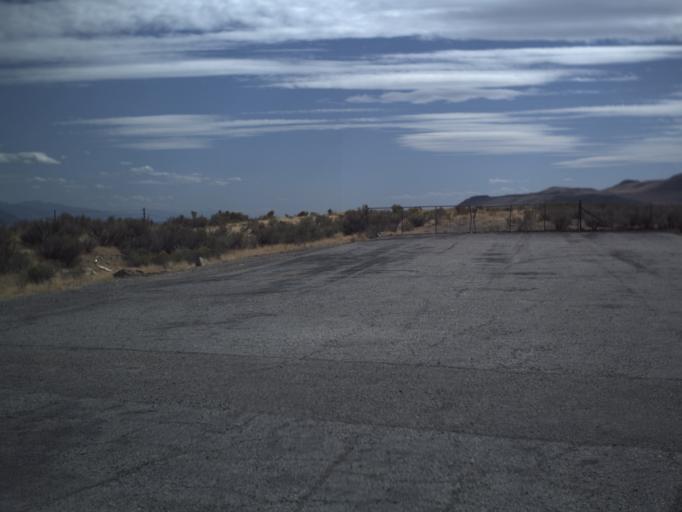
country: US
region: Utah
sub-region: Box Elder County
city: Tremonton
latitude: 41.7195
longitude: -112.2292
